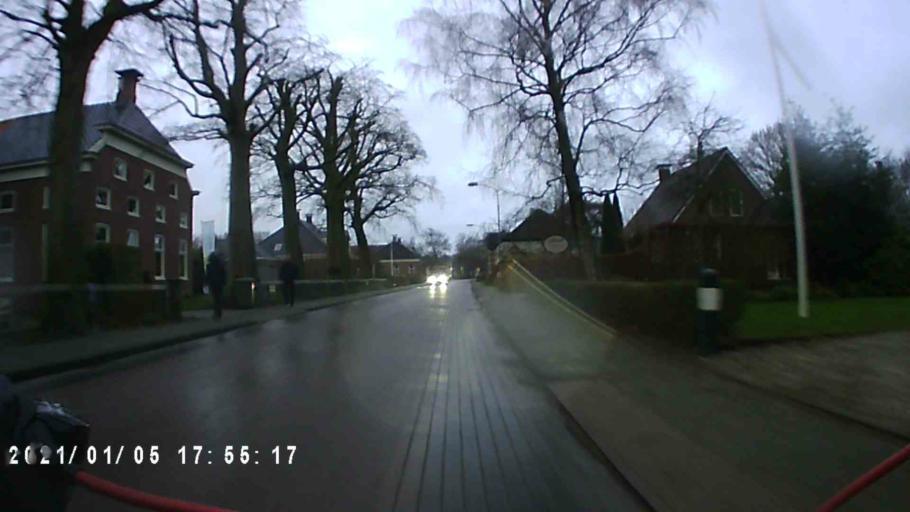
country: NL
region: Groningen
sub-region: Gemeente Slochteren
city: Slochteren
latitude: 53.2001
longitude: 6.8733
